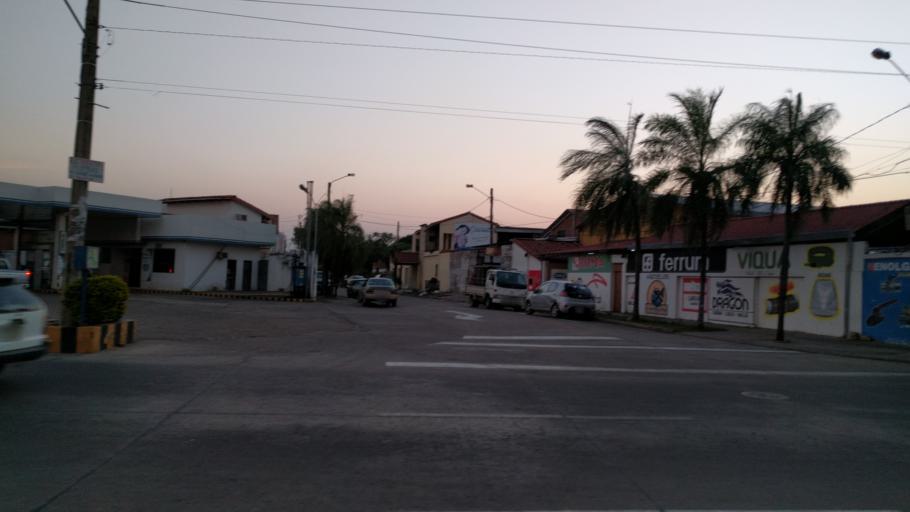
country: BO
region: Santa Cruz
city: Santa Cruz de la Sierra
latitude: -17.7701
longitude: -63.1569
